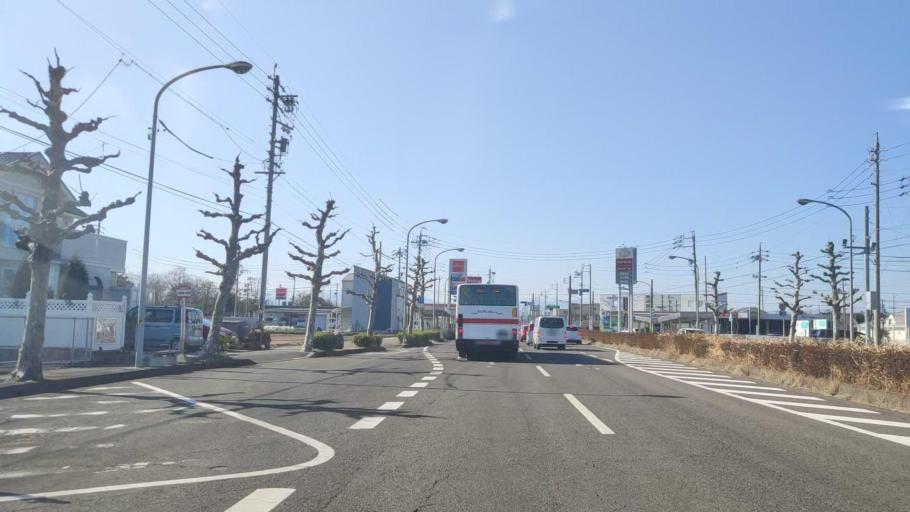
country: JP
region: Gifu
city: Gifu-shi
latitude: 35.4245
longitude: 136.7371
